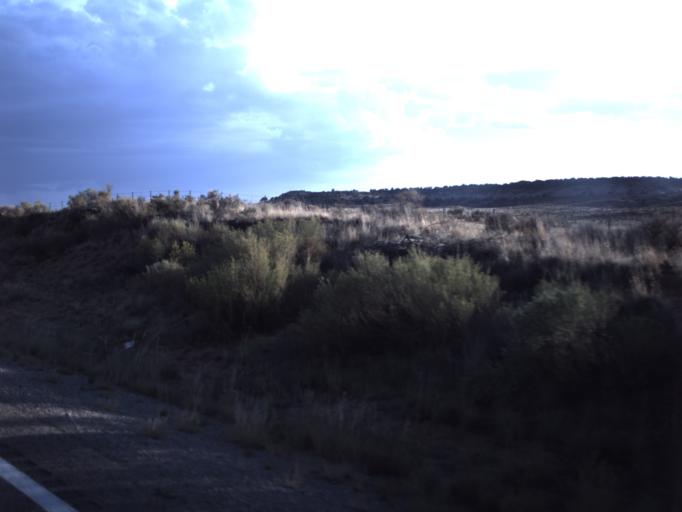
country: US
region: Utah
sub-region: San Juan County
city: Monticello
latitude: 38.1427
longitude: -109.3721
